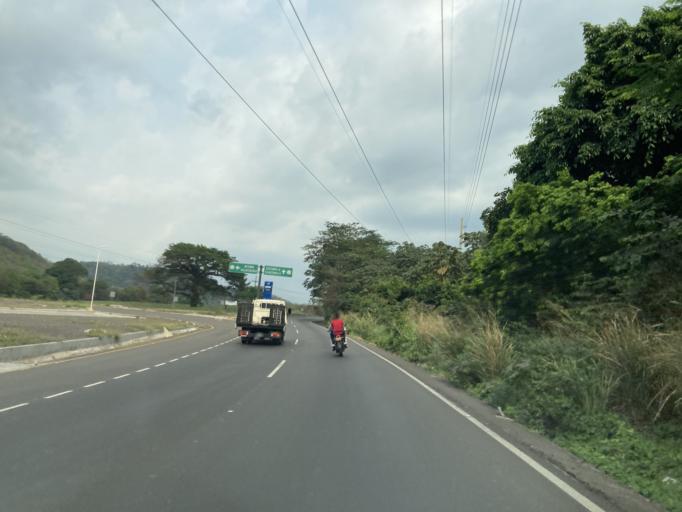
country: GT
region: Escuintla
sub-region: Municipio de La Democracia
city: La Democracia
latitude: 14.2666
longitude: -90.8878
